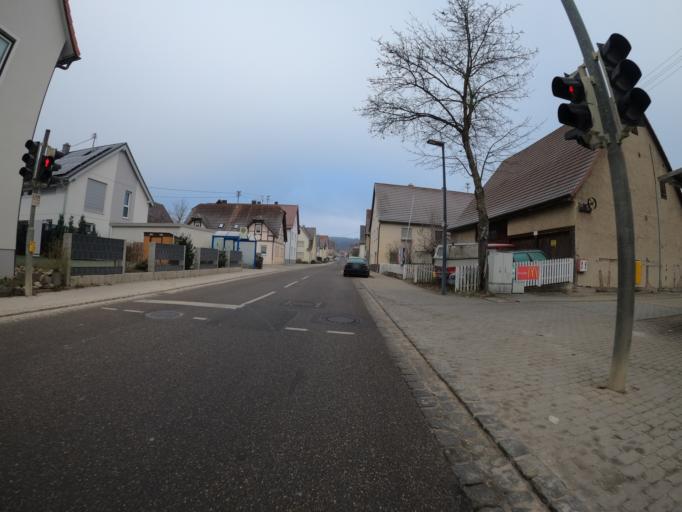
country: DE
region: Baden-Wuerttemberg
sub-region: Tuebingen Region
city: Westerstetten
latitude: 48.5192
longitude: 9.9532
